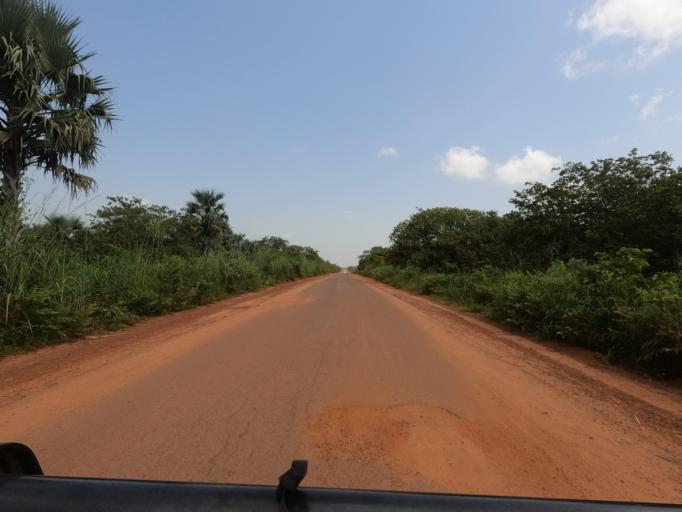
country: GW
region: Oio
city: Bissora
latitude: 12.2964
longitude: -15.7676
